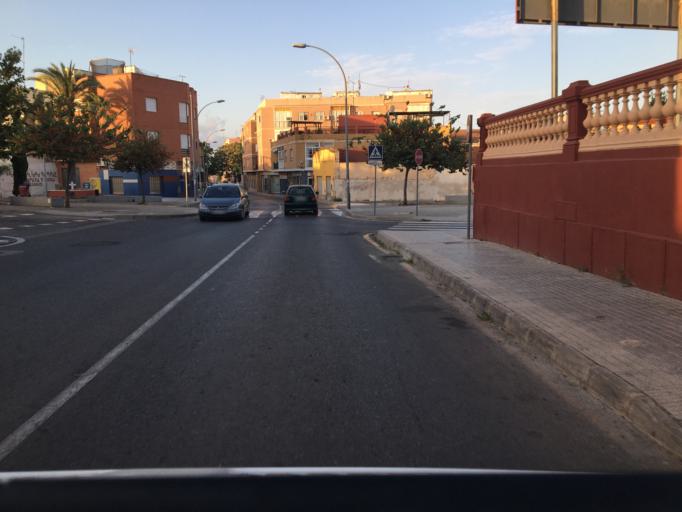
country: ES
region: Murcia
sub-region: Murcia
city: Cartagena
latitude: 37.6230
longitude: -0.9888
